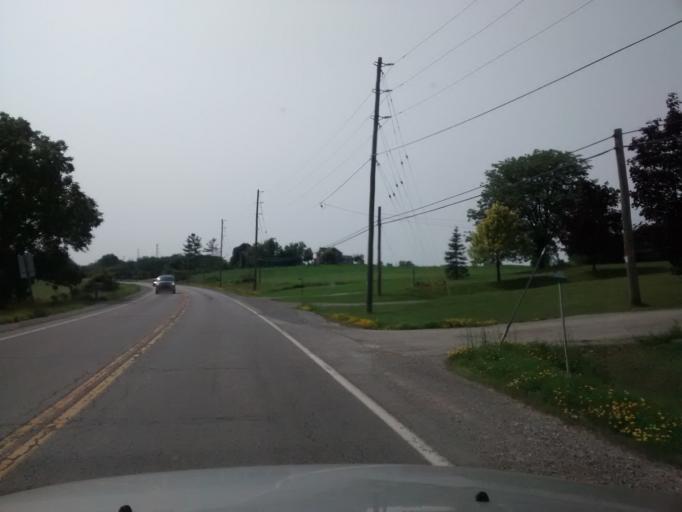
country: CA
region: Ontario
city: Ancaster
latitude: 43.0629
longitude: -79.9231
